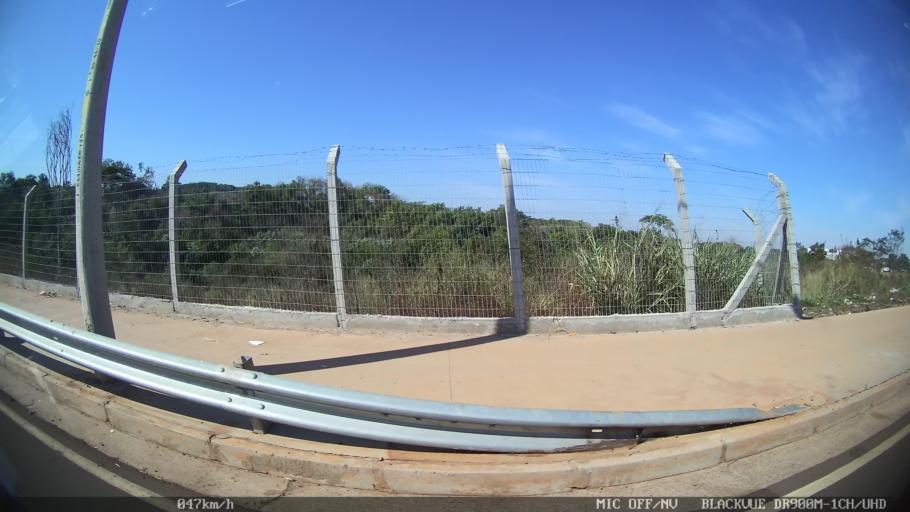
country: BR
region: Sao Paulo
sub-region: Sao Jose Do Rio Preto
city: Sao Jose do Rio Preto
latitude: -20.7637
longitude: -49.3773
